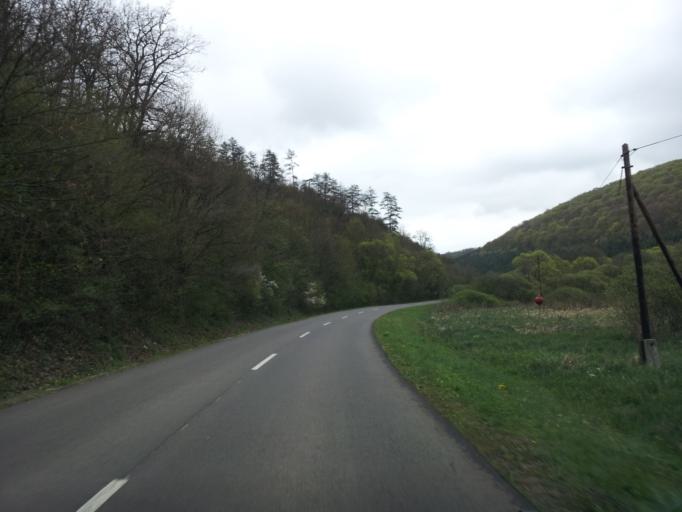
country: HU
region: Borsod-Abauj-Zemplen
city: Rudabanya
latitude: 48.4788
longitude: 20.5829
